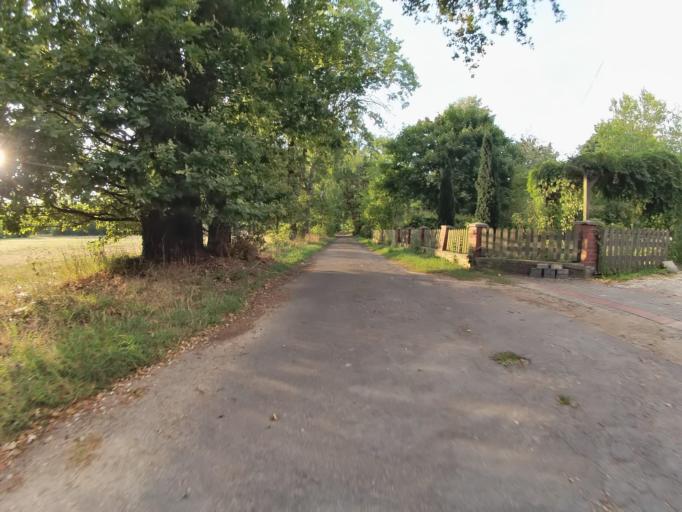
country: DE
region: North Rhine-Westphalia
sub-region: Regierungsbezirk Munster
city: Westerkappeln
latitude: 52.3633
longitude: 7.8950
